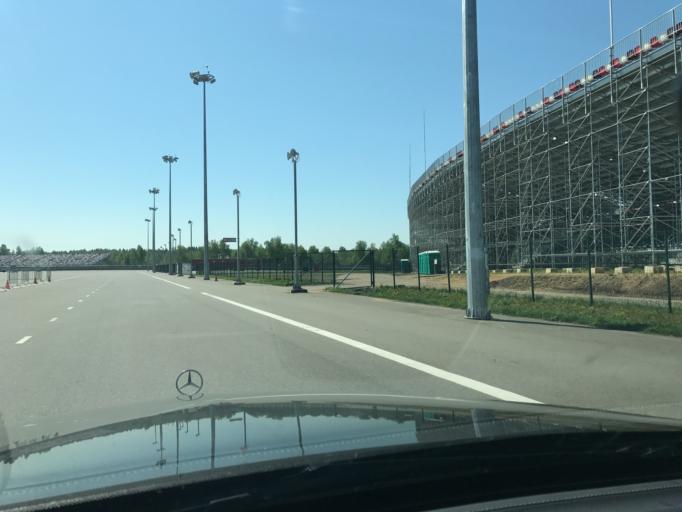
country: RU
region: Moskovskaya
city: Sychevo
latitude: 55.9968
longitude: 36.2687
